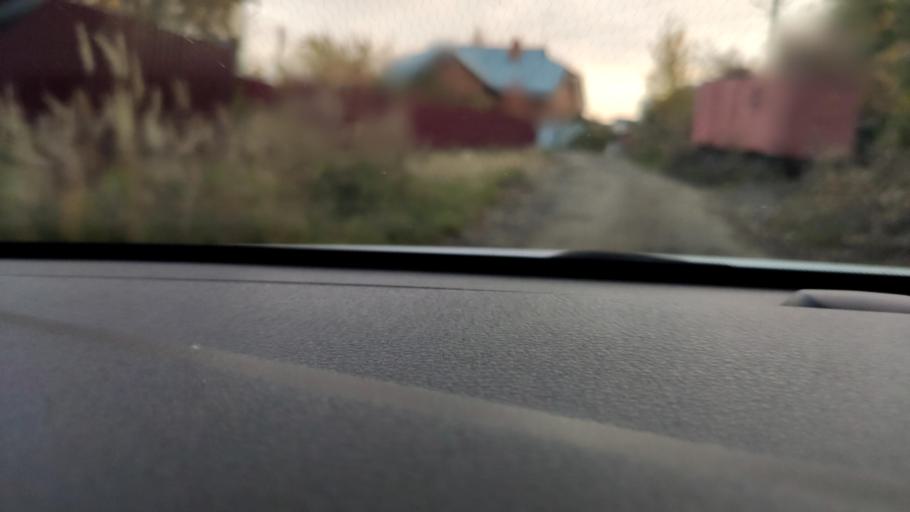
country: RU
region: Tatarstan
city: Stolbishchi
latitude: 55.7586
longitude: 49.2480
